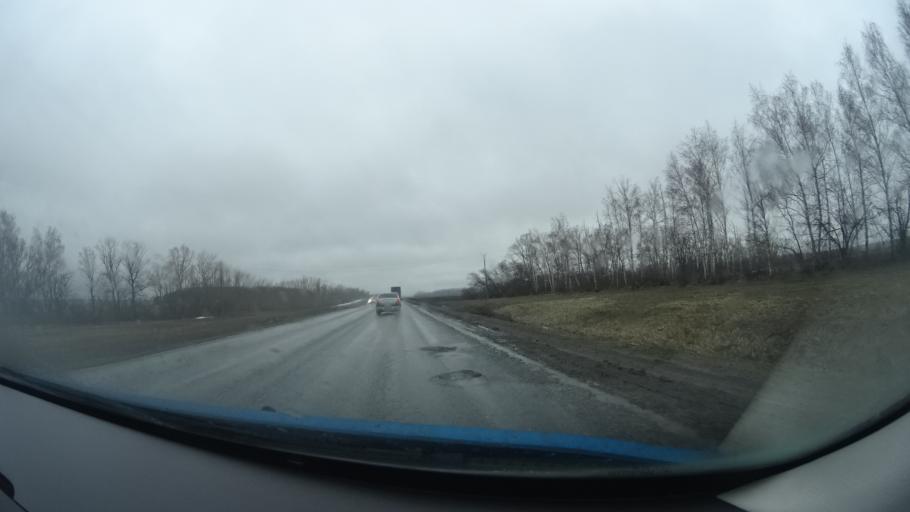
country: RU
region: Bashkortostan
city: Buzdyak
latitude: 54.6157
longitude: 54.3462
